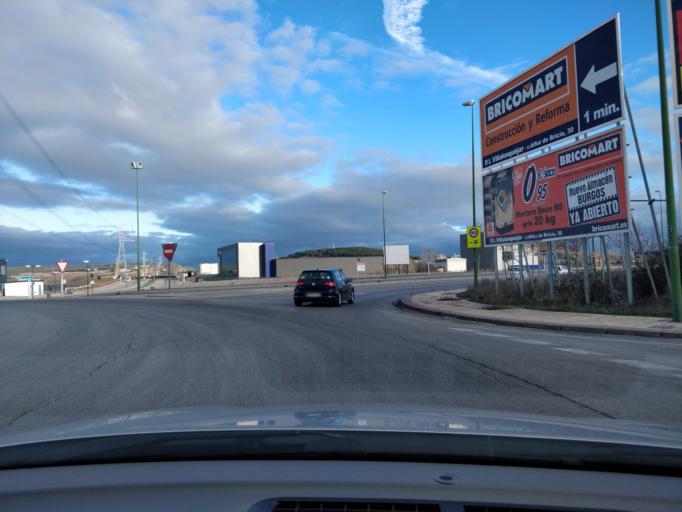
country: ES
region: Castille and Leon
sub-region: Provincia de Burgos
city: Burgos
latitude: 42.3630
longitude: -3.7113
